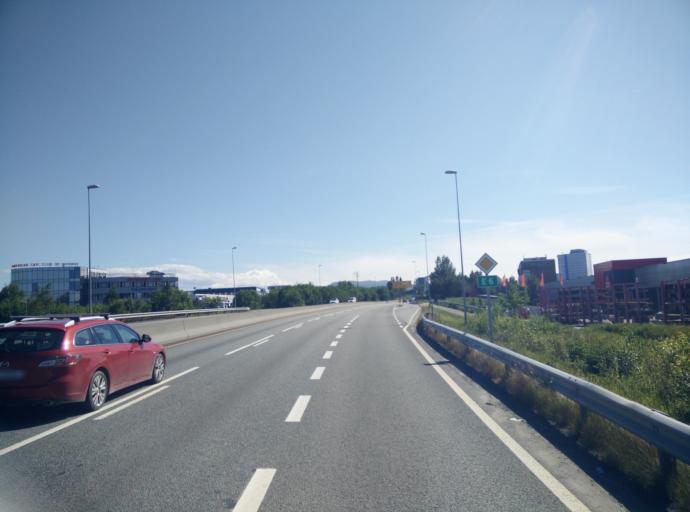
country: NO
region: Sor-Trondelag
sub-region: Trondheim
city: Trondheim
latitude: 63.3699
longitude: 10.3794
